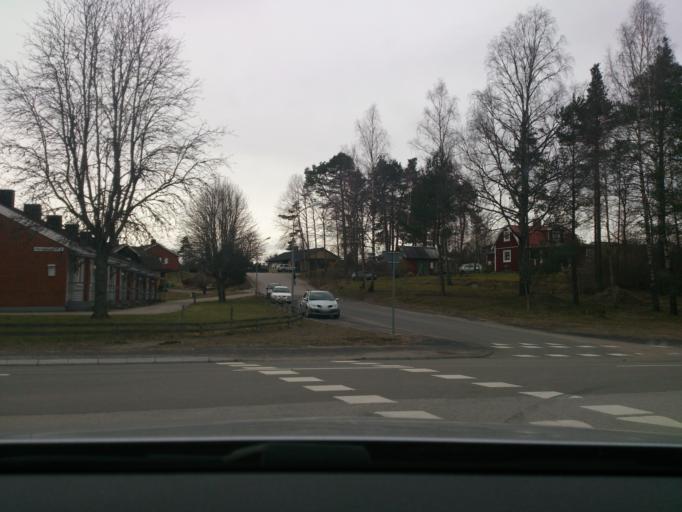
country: SE
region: Kronoberg
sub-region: Alvesta Kommun
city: Moheda
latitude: 57.0076
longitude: 14.5722
